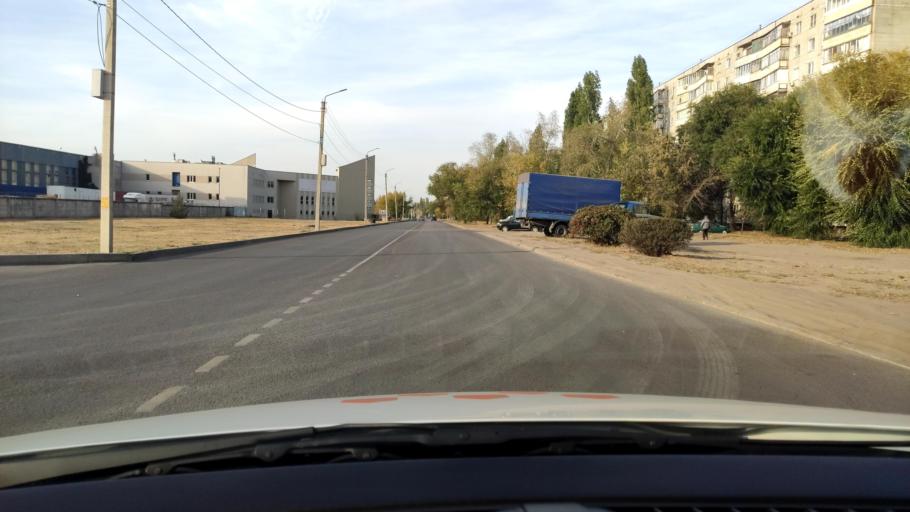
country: RU
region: Voronezj
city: Maslovka
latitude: 51.5954
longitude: 39.2369
